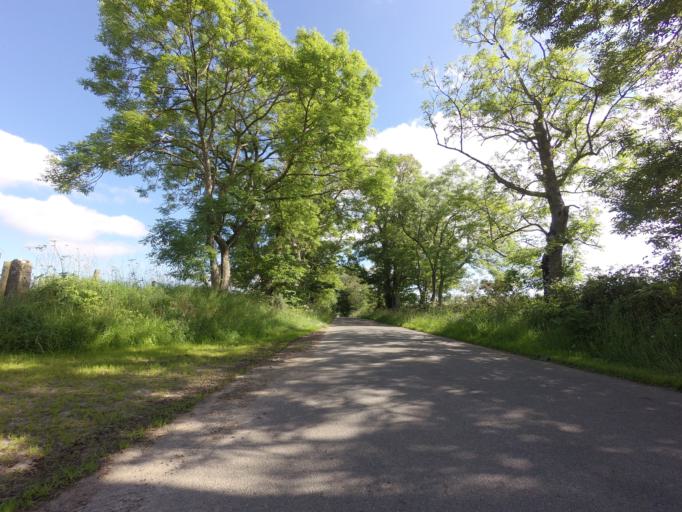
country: GB
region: Scotland
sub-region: Aberdeenshire
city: Turriff
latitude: 57.5910
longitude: -2.5059
